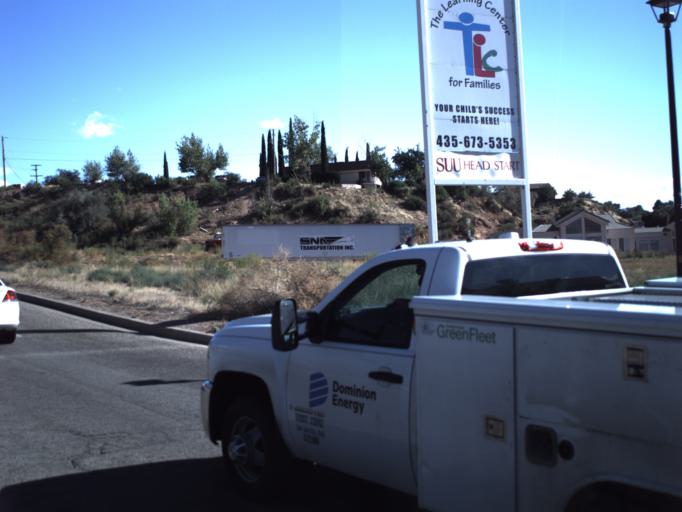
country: US
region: Utah
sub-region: Washington County
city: LaVerkin
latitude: 37.2165
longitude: -113.2731
